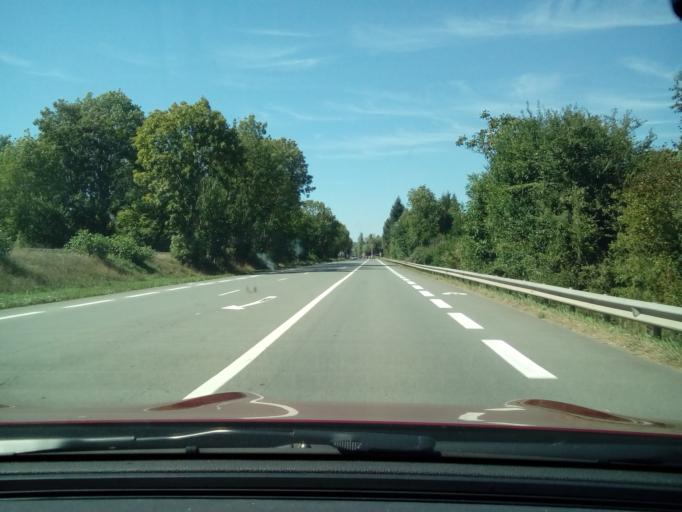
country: FR
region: Rhone-Alpes
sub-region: Departement du Rhone
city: Charnay
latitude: 45.8729
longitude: 4.6492
